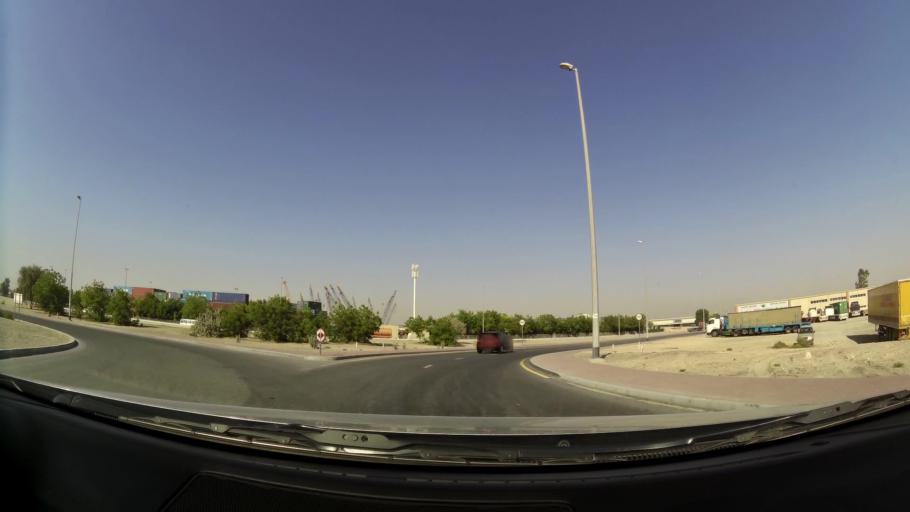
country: AE
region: Dubai
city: Dubai
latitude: 24.9924
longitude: 55.1054
